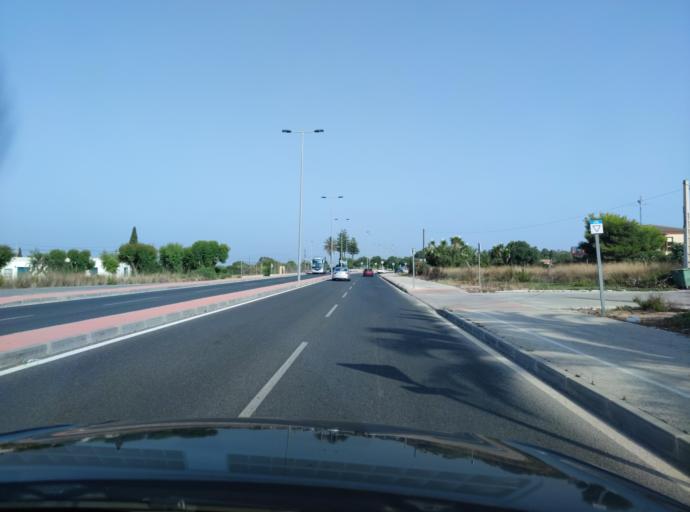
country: ES
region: Valencia
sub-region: Provincia de Alicante
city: Santa Pola
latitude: 38.2044
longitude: -0.5781
